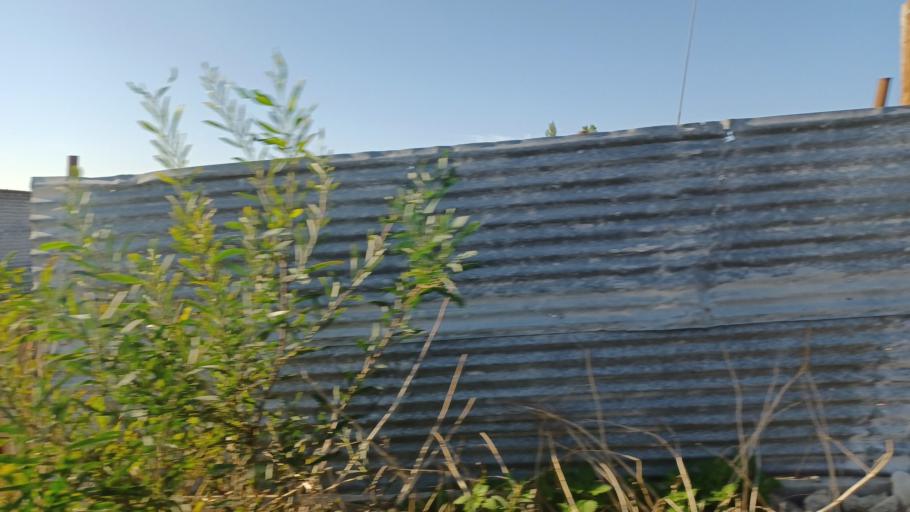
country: CY
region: Larnaka
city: Psevdas
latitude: 34.9377
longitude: 33.5263
